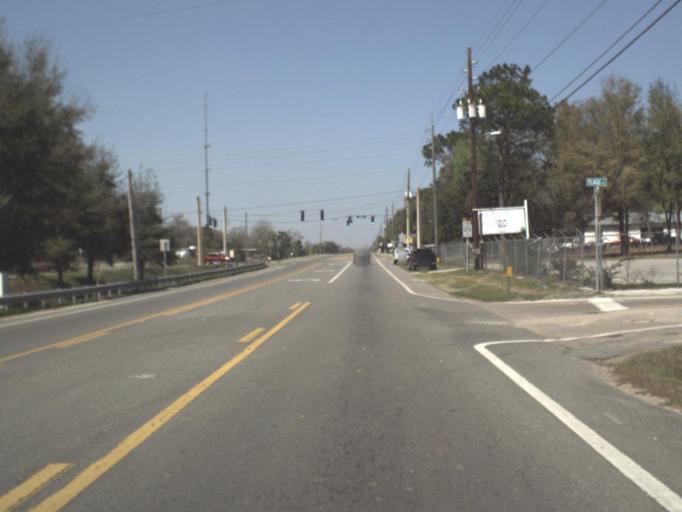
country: US
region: Florida
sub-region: Leon County
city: Tallahassee
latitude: 30.3804
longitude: -84.2722
